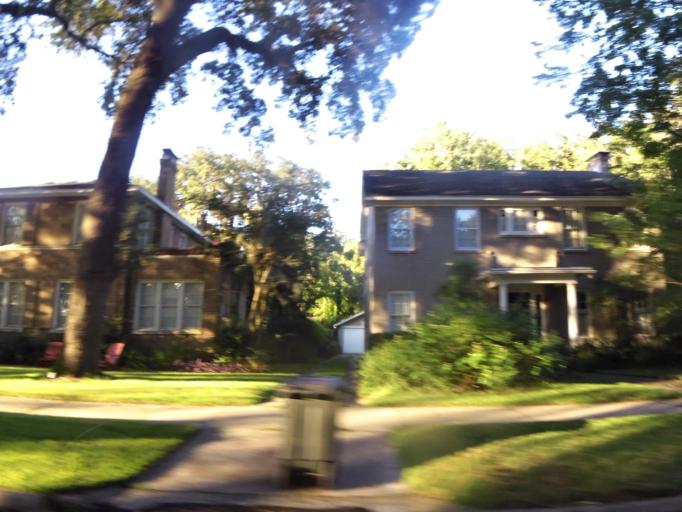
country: US
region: Florida
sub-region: Duval County
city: Jacksonville
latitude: 30.3006
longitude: -81.7031
